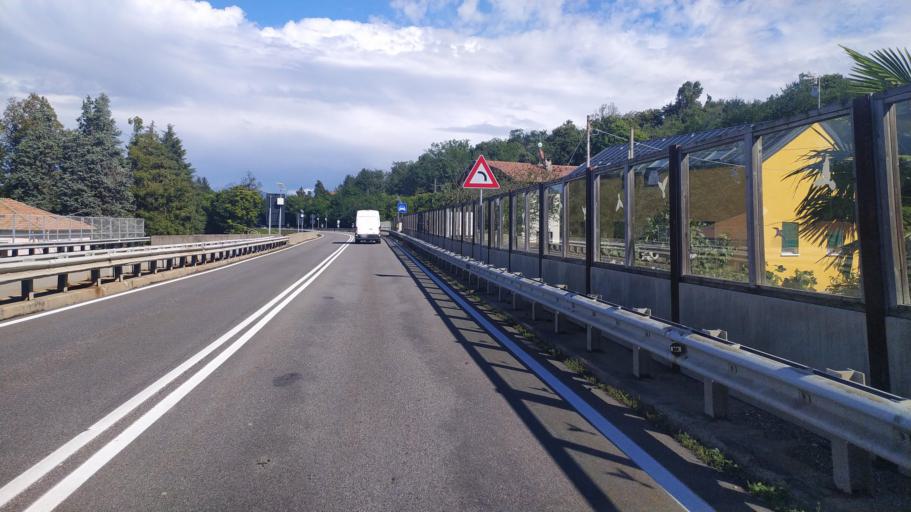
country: IT
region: Lombardy
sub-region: Provincia di Varese
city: Gazzada Schianno
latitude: 45.7889
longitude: 8.8283
